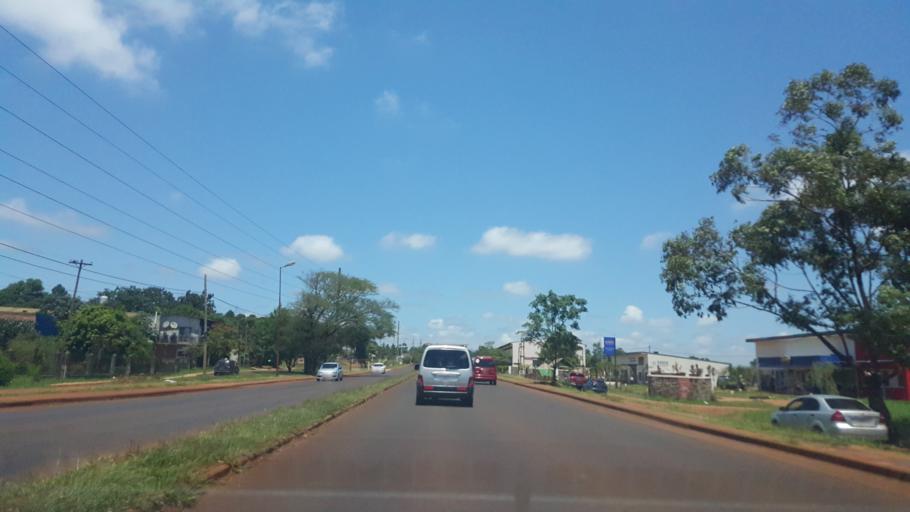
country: AR
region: Misiones
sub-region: Departamento de Capital
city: Posadas
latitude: -27.4194
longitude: -55.9309
